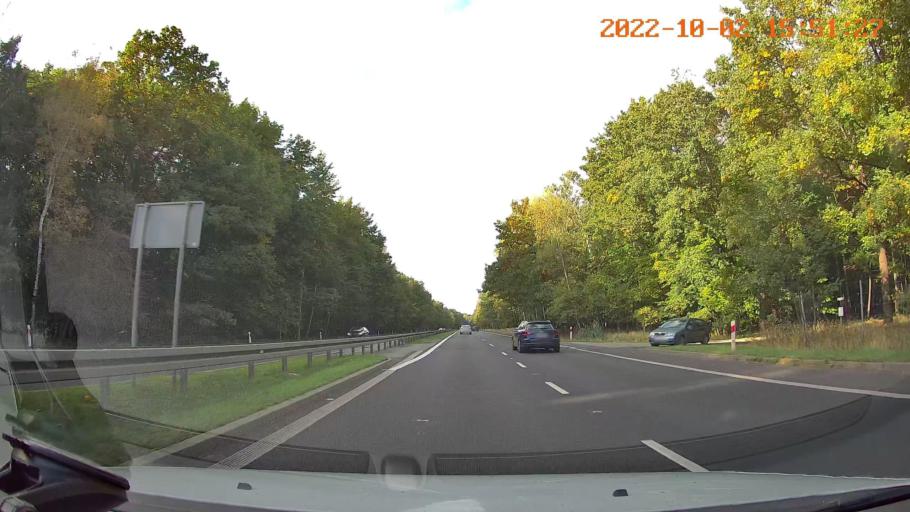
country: PL
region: Silesian Voivodeship
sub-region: Tychy
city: Cielmice
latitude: 50.1409
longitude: 19.0248
